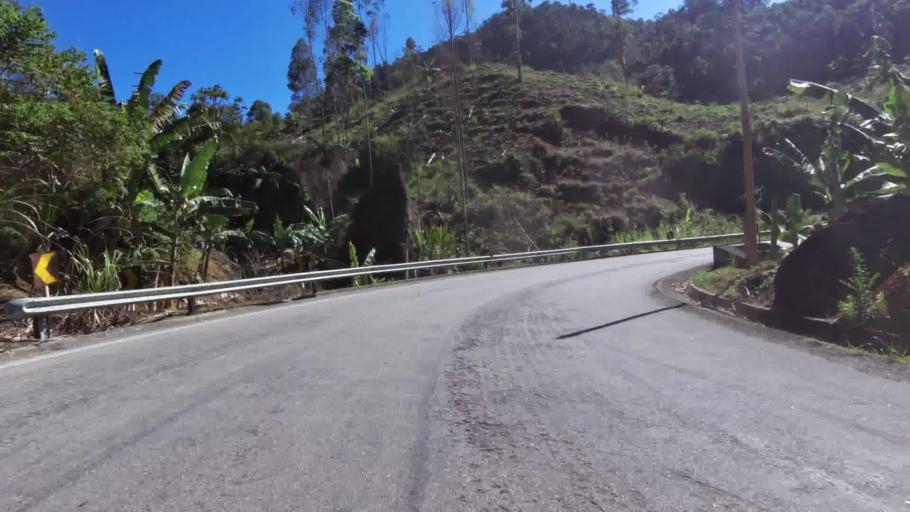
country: BR
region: Espirito Santo
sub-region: Vargem Alta
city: Vargem Alta
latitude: -20.6945
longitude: -40.9368
